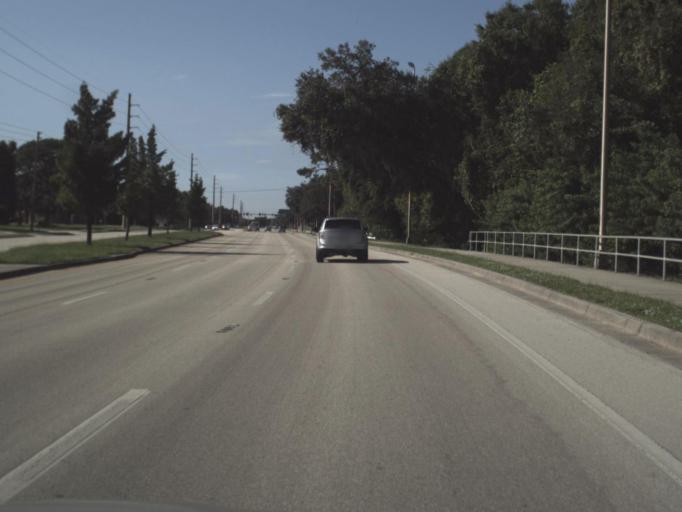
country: US
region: Florida
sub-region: Sarasota County
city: South Venice
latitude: 27.0179
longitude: -82.3870
